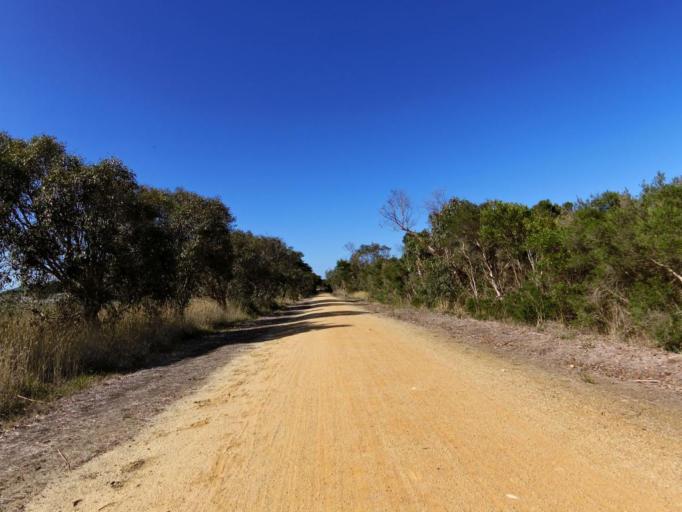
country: AU
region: Victoria
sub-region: Bass Coast
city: North Wonthaggi
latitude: -38.5864
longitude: 145.5564
